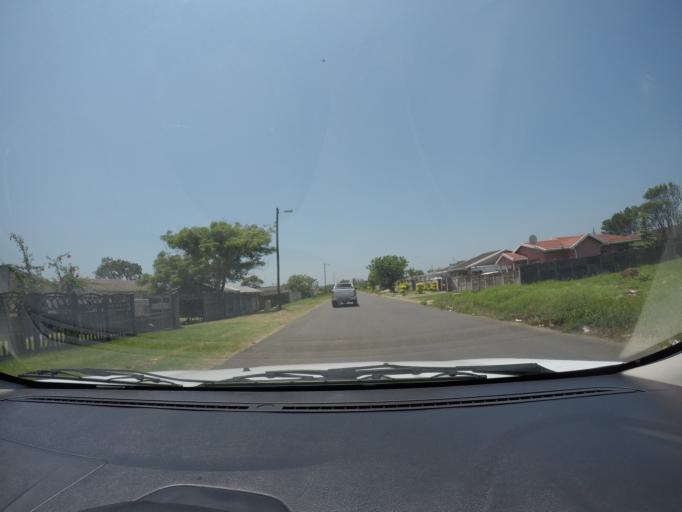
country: ZA
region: KwaZulu-Natal
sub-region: uThungulu District Municipality
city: eSikhawini
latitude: -28.8803
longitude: 31.8913
